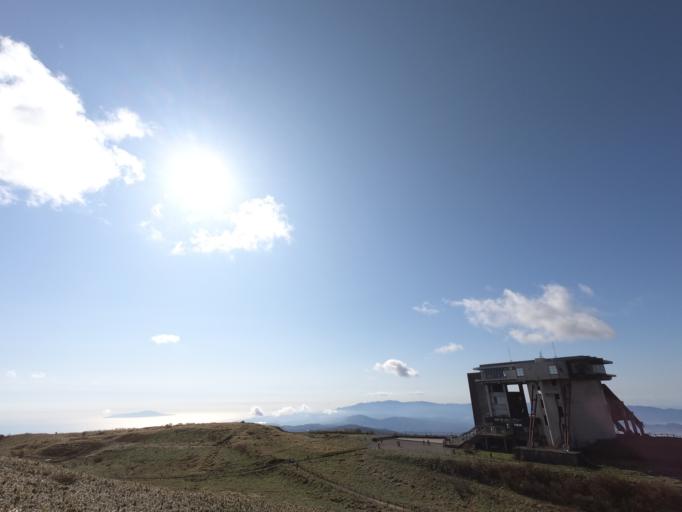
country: JP
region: Kanagawa
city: Hakone
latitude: 35.2246
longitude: 139.0246
